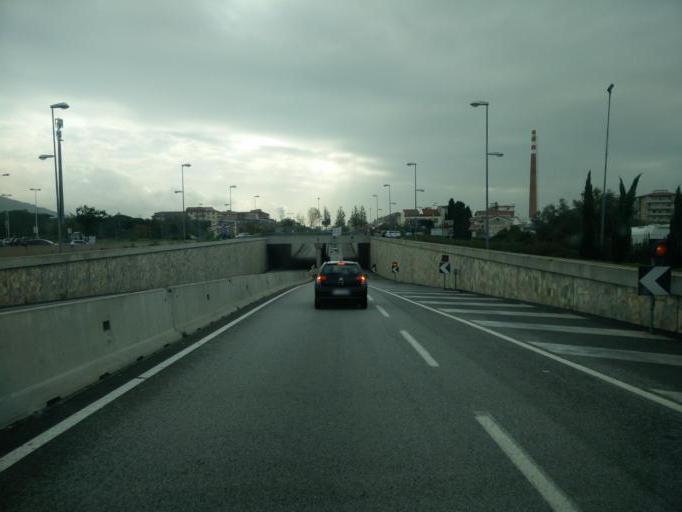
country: IT
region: Tuscany
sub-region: Provincia di Prato
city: Prato
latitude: 43.8738
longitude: 11.0806
